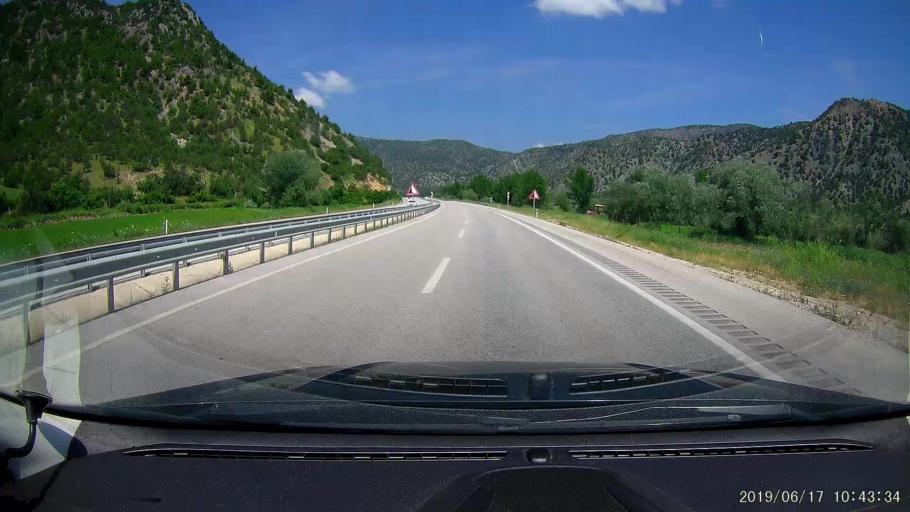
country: TR
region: Corum
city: Kargi
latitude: 41.0664
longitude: 34.5332
